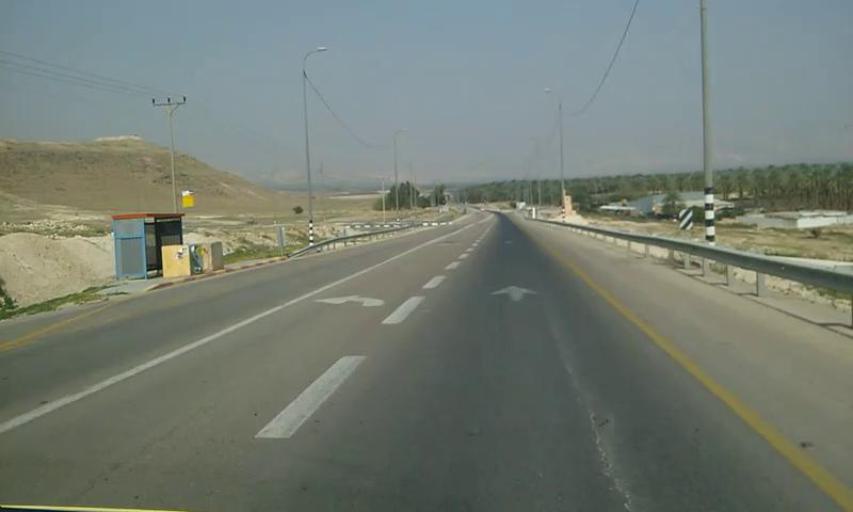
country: PS
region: West Bank
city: Al `Awja
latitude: 31.9744
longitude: 35.4691
